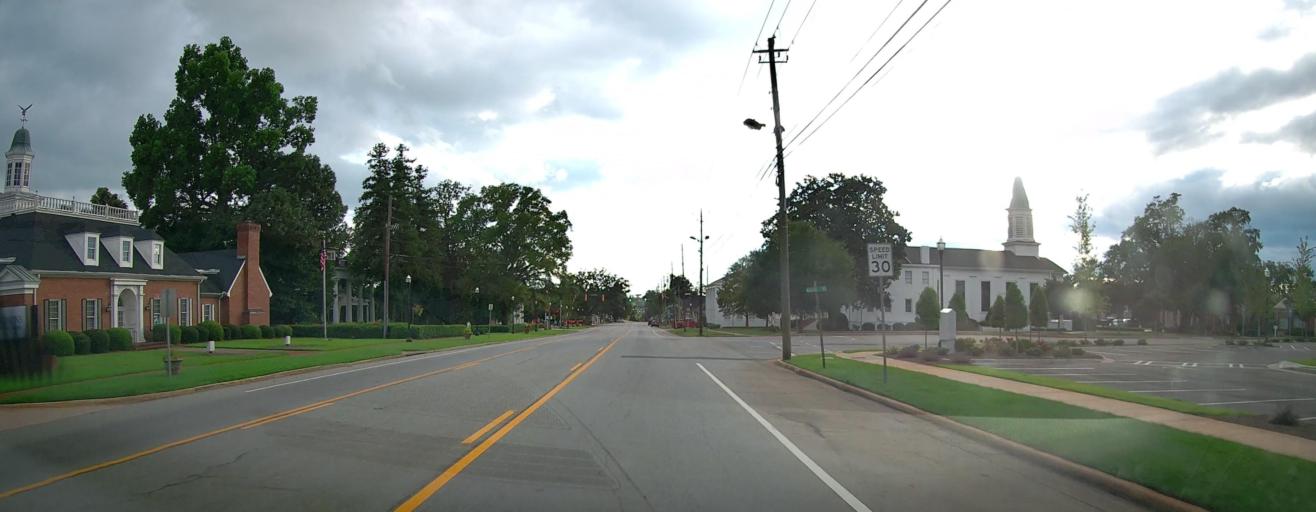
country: US
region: Georgia
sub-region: Houston County
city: Perry
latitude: 32.4585
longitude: -83.7305
